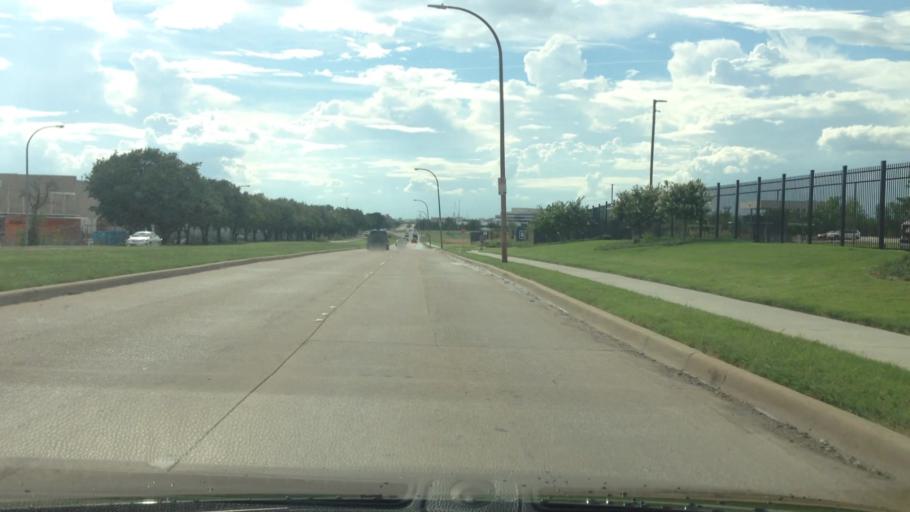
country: US
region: Texas
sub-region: Tarrant County
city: Haltom City
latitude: 32.8244
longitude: -97.2936
